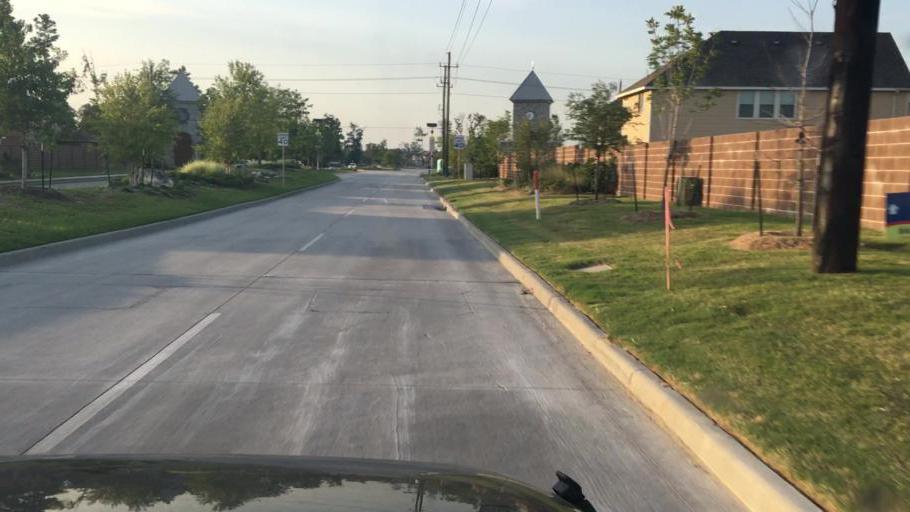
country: US
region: Texas
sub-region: Harris County
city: Atascocita
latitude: 29.9401
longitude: -95.2114
